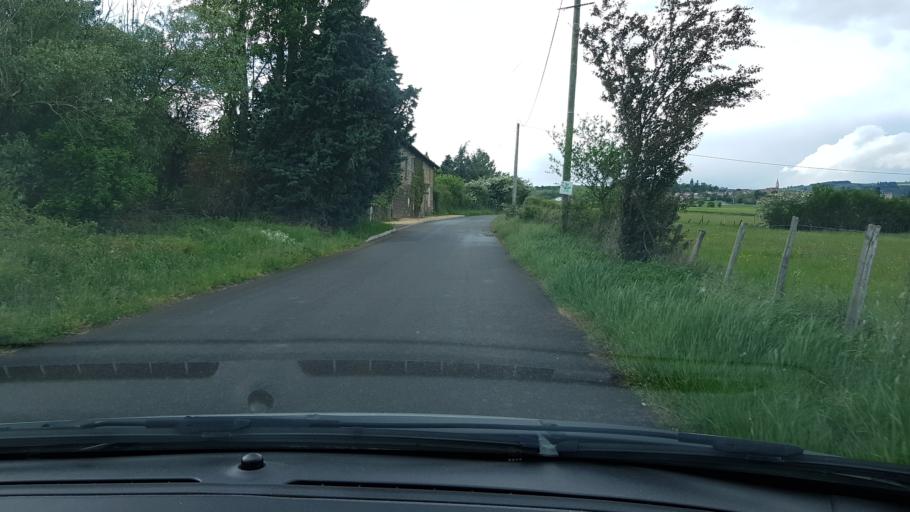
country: FR
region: Rhone-Alpes
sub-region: Departement du Rhone
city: Saint-Maurice-sur-Dargoire
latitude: 45.5732
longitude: 4.6466
